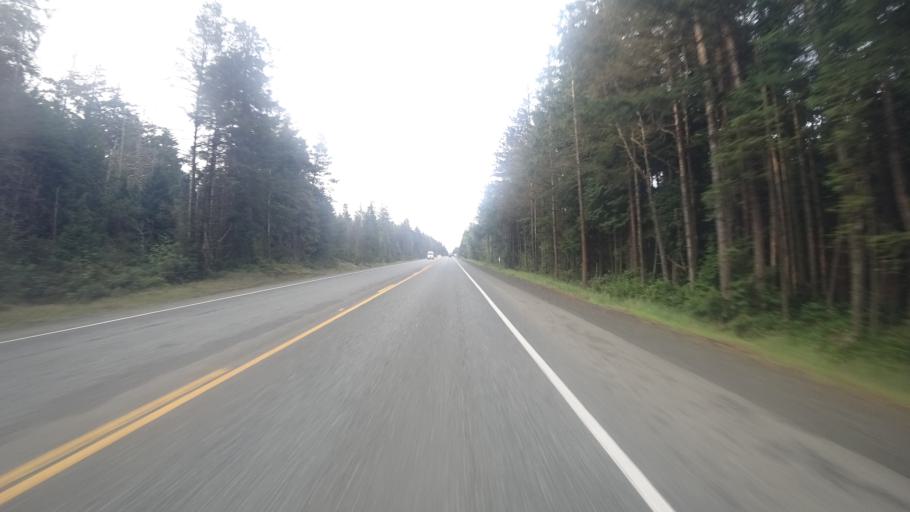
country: US
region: Oregon
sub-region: Coos County
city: Lakeside
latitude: 43.5181
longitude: -124.2169
